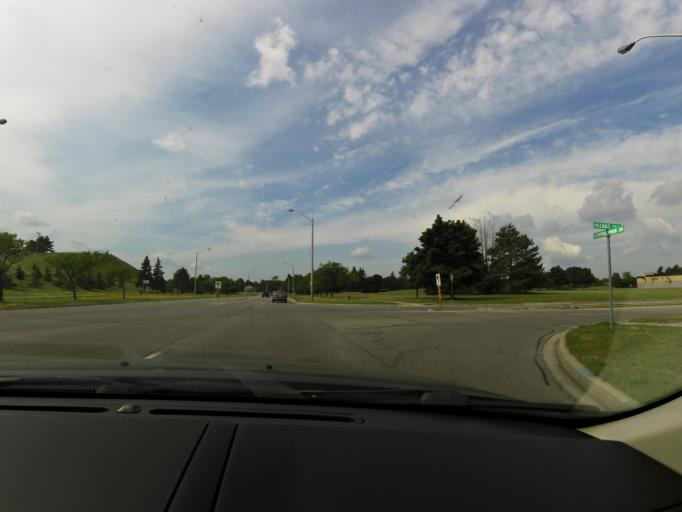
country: CA
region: Ontario
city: Brampton
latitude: 43.7289
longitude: -79.7257
